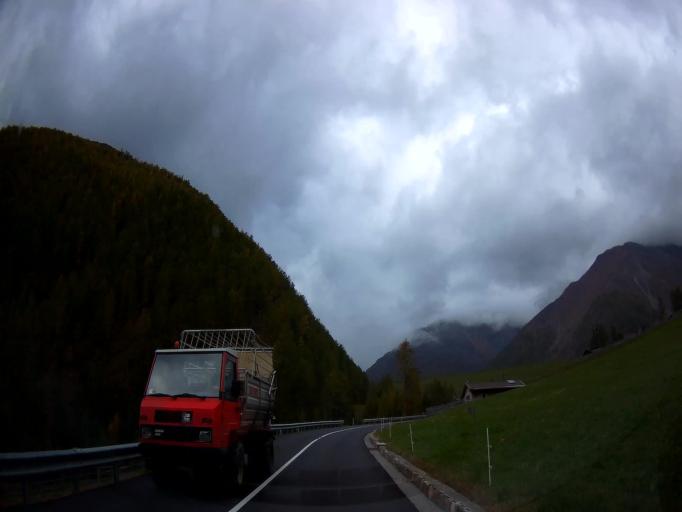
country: IT
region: Trentino-Alto Adige
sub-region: Bolzano
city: Senales
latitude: 46.7296
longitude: 10.8538
